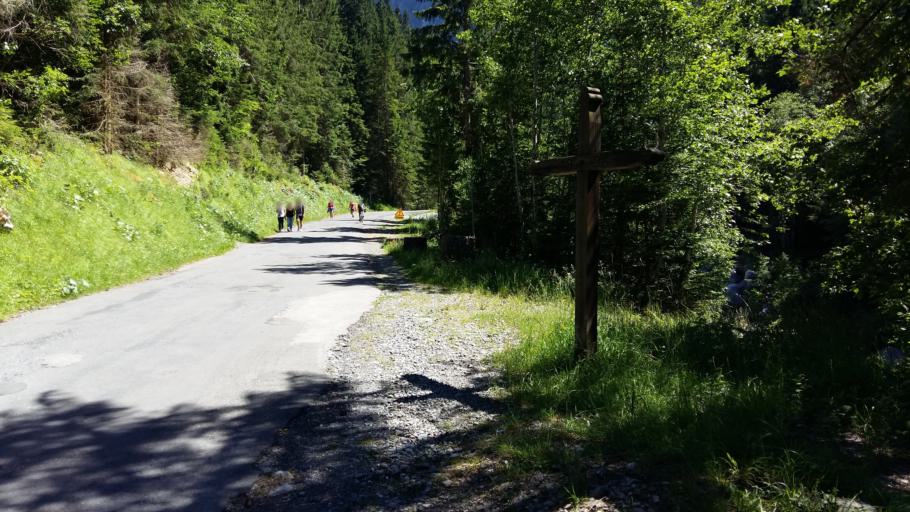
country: FR
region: Rhone-Alpes
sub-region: Departement de la Haute-Savoie
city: Samoens
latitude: 46.0337
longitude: 6.7720
